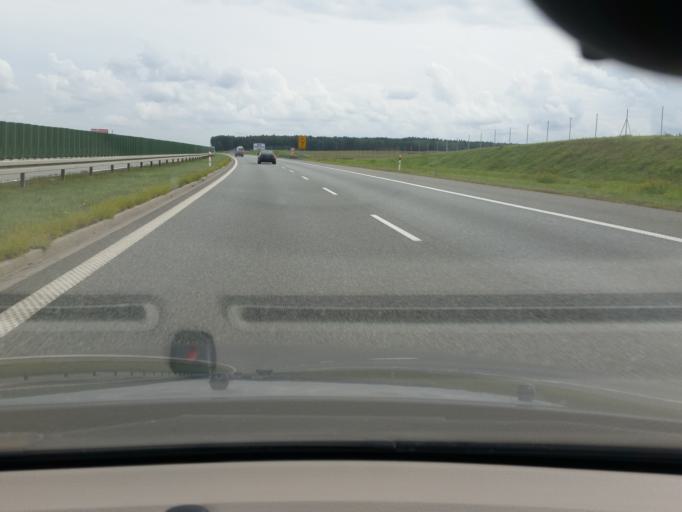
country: PL
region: Pomeranian Voivodeship
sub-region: Powiat gdanski
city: Legowo
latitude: 54.2068
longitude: 18.6169
